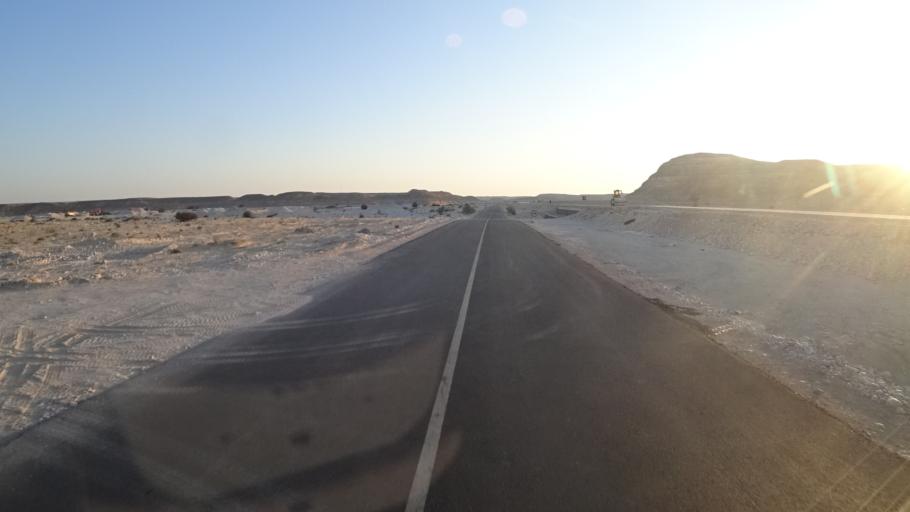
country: OM
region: Zufar
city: Salalah
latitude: 17.5216
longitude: 53.3773
